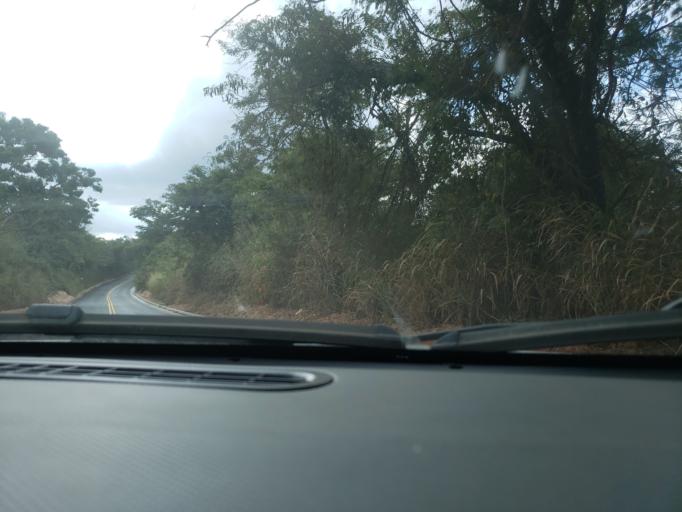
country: BR
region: Minas Gerais
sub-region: Campo Belo
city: Campo Belo
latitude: -20.9178
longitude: -45.2942
